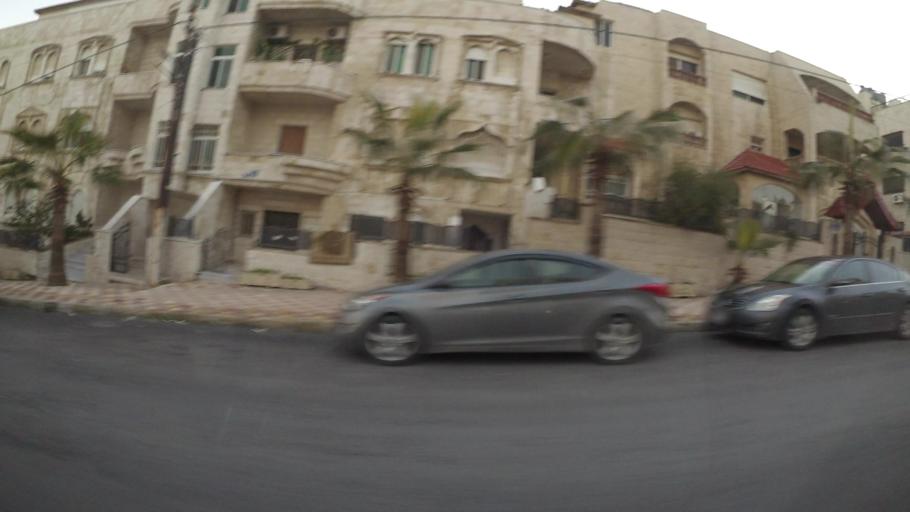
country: JO
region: Amman
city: Al Jubayhah
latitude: 31.9980
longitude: 35.8565
